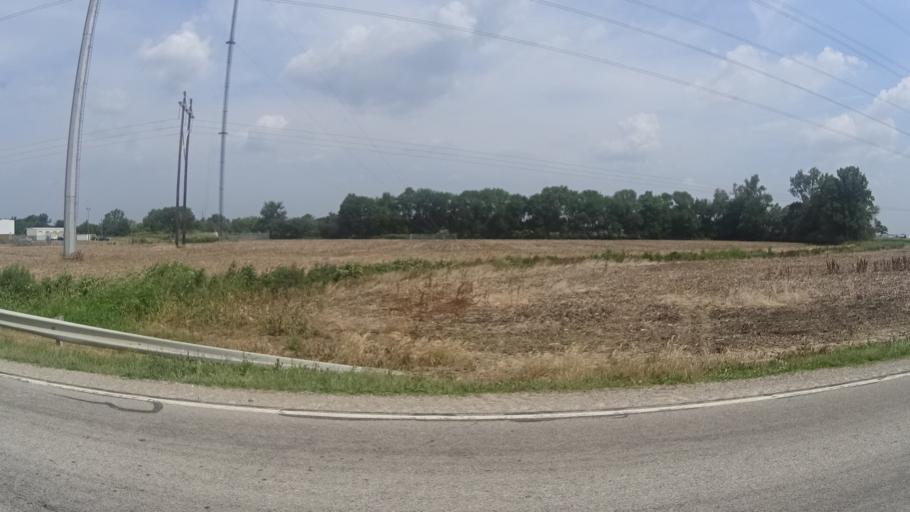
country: US
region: Ohio
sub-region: Erie County
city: Milan
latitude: 41.3337
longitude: -82.6409
